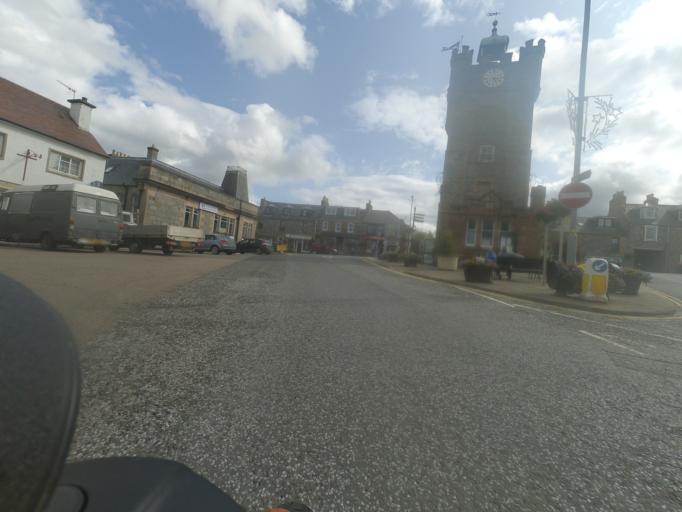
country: GB
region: Scotland
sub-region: Moray
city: Dufftown
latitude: 57.4451
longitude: -3.1283
